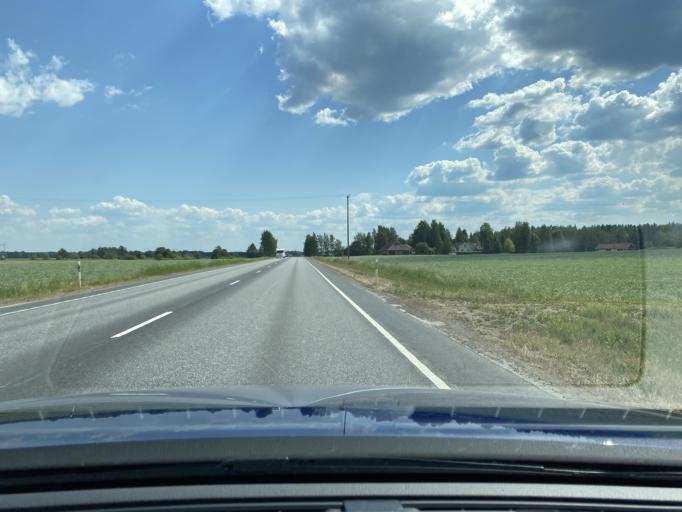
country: FI
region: Satakunta
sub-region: Rauma
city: Eura
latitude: 61.1523
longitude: 22.0971
